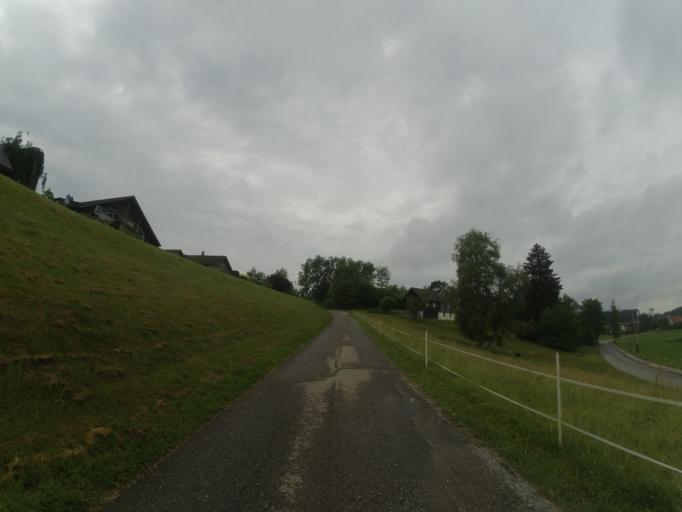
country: DE
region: Baden-Wuerttemberg
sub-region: Tuebingen Region
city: Kisslegg
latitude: 47.7817
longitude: 9.8774
